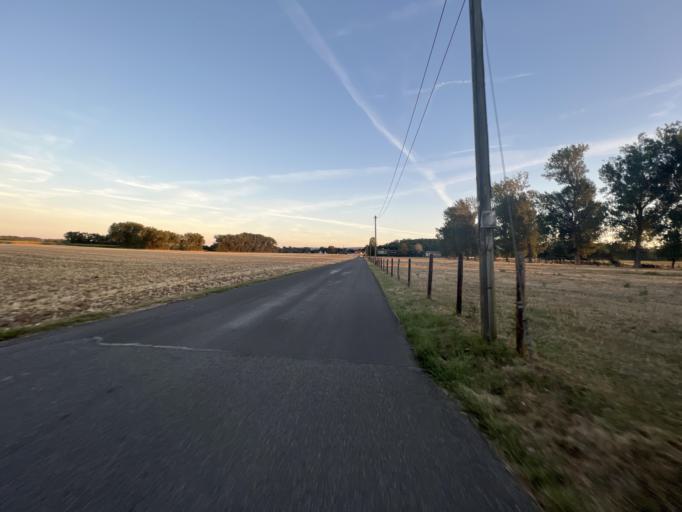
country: DE
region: North Rhine-Westphalia
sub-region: Regierungsbezirk Koln
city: Langerwehe
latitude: 50.8170
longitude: 6.4206
